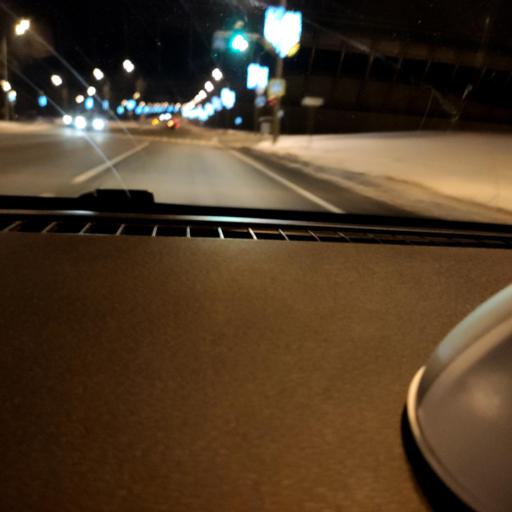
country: RU
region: Samara
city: Petra-Dubrava
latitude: 53.3070
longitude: 50.2380
